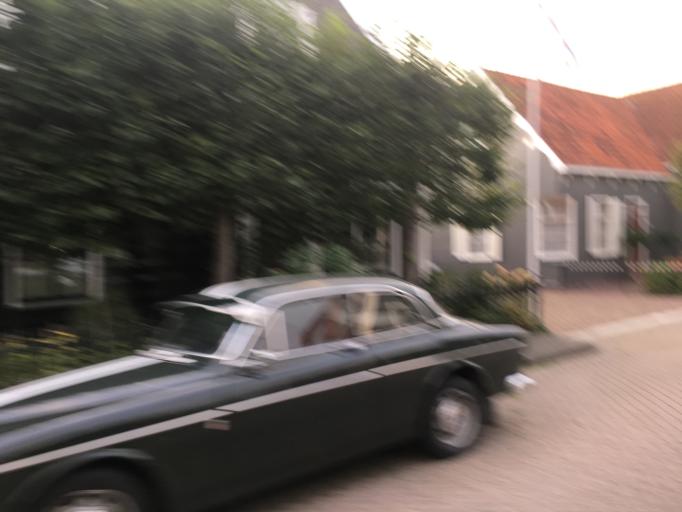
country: NL
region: North Holland
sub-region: Gemeente Zaanstad
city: Zaanstad
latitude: 52.4517
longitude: 4.7757
